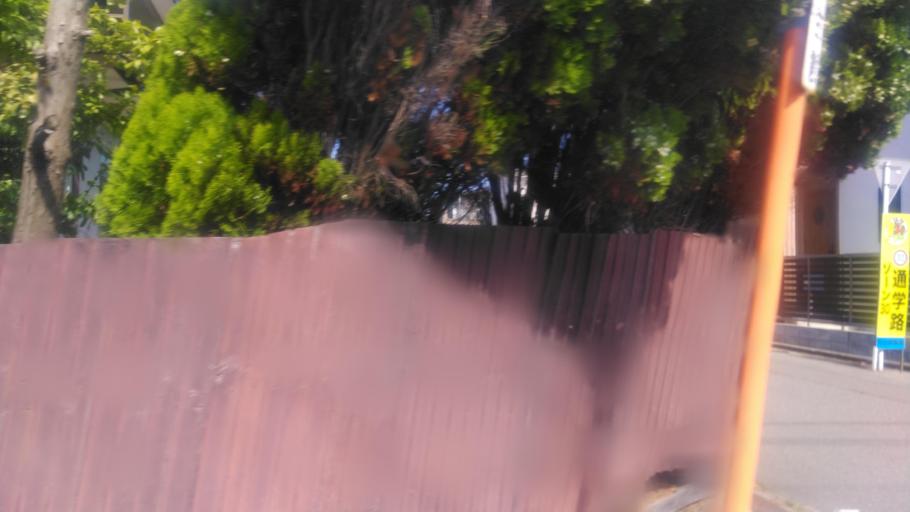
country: JP
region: Akita
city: Noshiromachi
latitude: 40.2040
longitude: 140.0237
